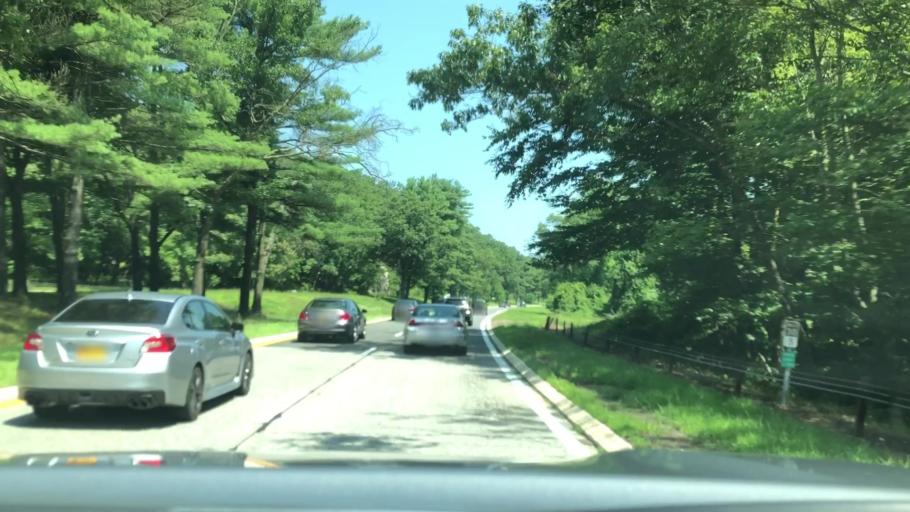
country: US
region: New York
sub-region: Rockland County
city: Thiells
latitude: 41.2560
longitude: -74.0443
